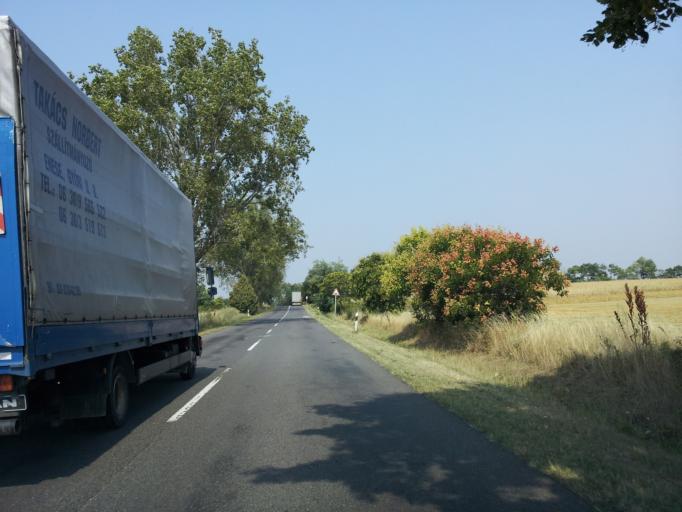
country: HU
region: Gyor-Moson-Sopron
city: Pannonhalma
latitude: 47.4830
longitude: 17.7868
